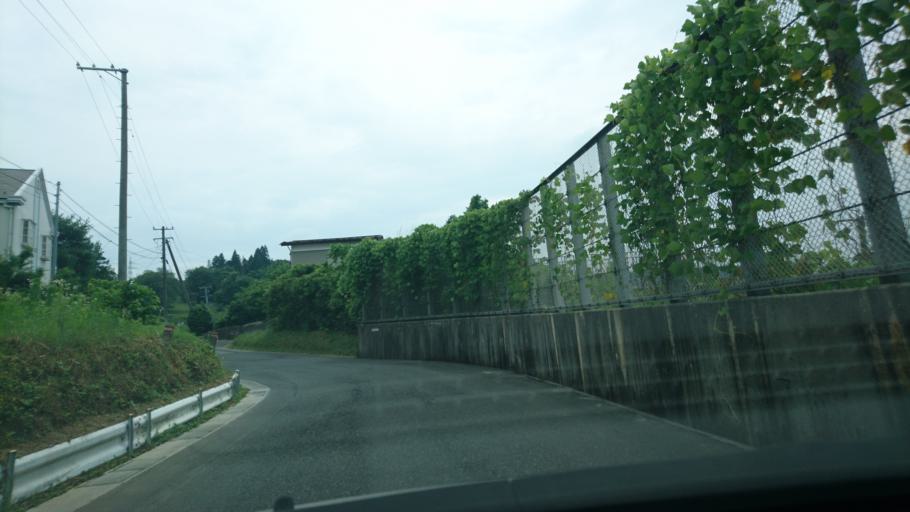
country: JP
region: Iwate
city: Ichinoseki
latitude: 38.9179
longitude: 141.1357
